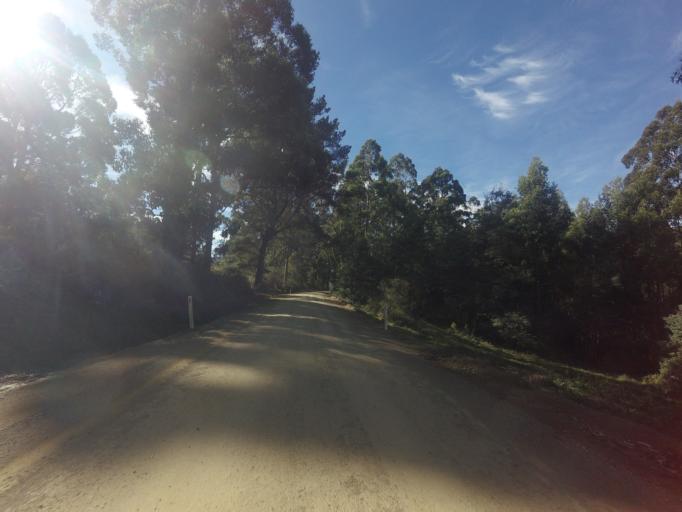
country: AU
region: Tasmania
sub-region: Clarence
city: Sandford
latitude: -43.1414
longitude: 147.7665
